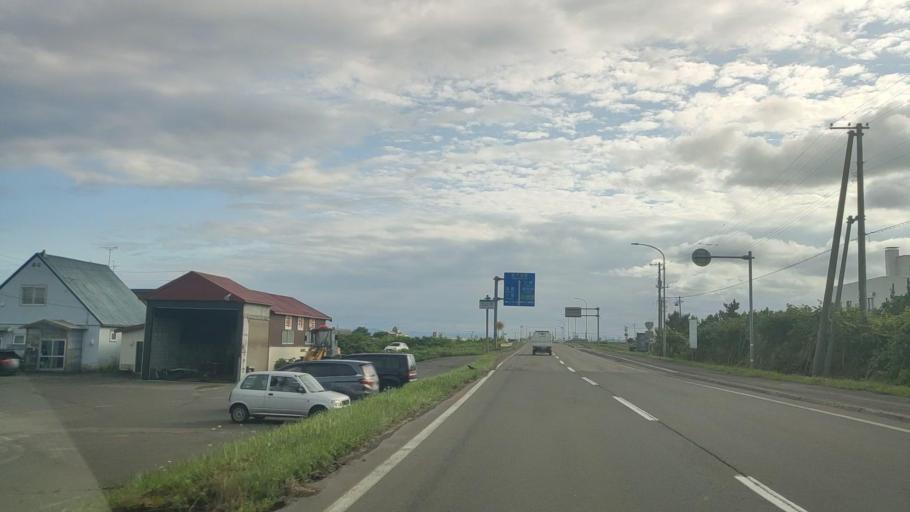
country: JP
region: Hokkaido
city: Niseko Town
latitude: 42.5207
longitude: 140.3835
